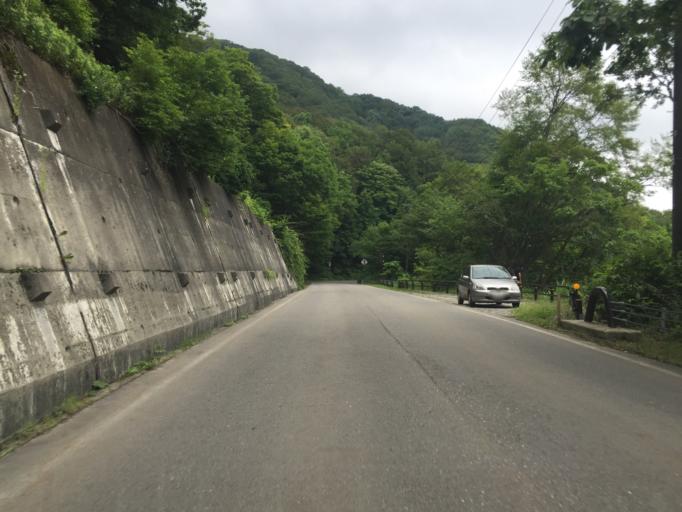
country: JP
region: Fukushima
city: Inawashiro
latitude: 37.7065
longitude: 140.0628
